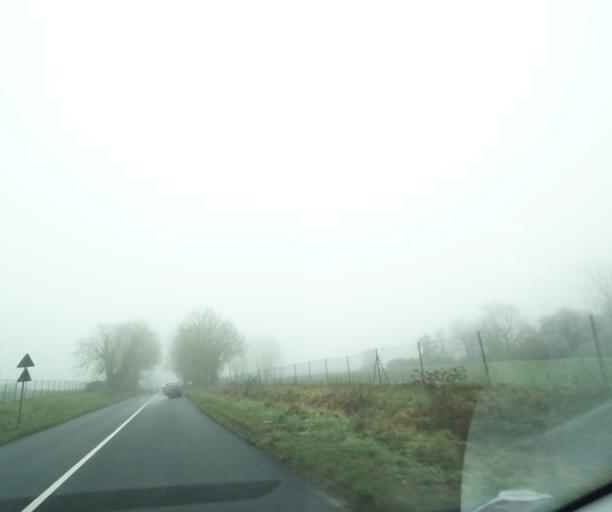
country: FR
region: Ile-de-France
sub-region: Departement de Seine-et-Marne
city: Dammartin-en-Goele
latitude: 49.0490
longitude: 2.6738
